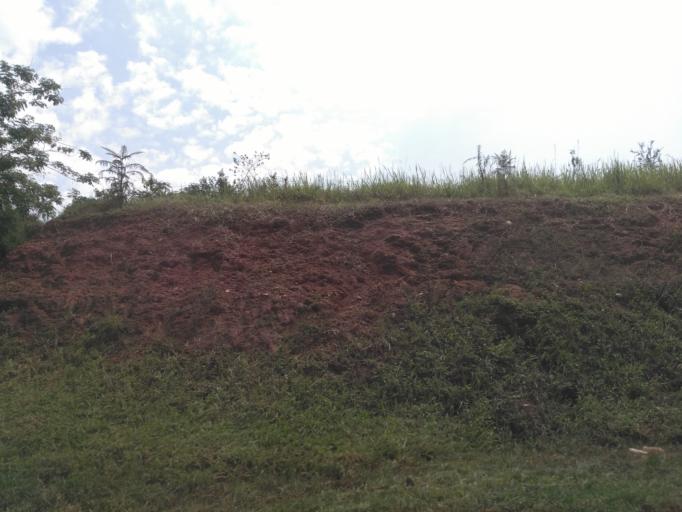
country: UG
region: Central Region
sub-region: Wakiso District
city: Bweyogerere
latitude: 0.4829
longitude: 32.6087
